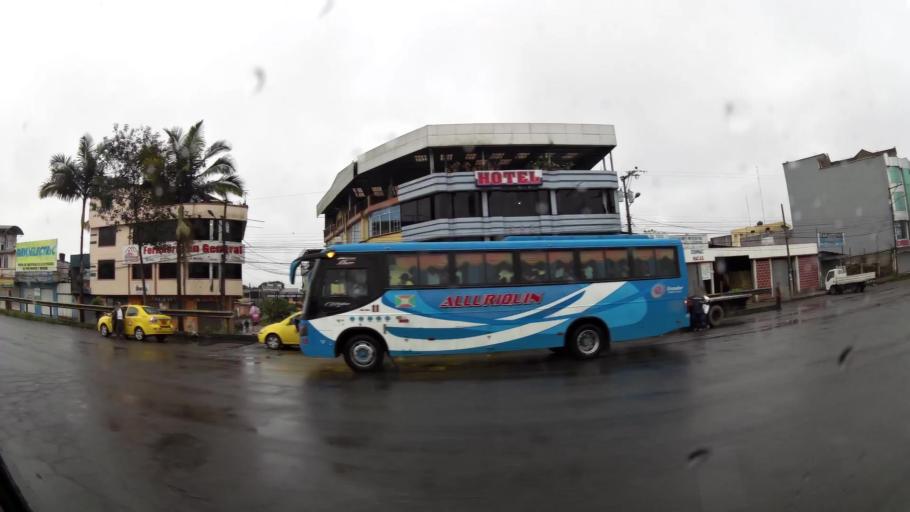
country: EC
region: Santo Domingo de los Tsachilas
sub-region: Canton Santo Domingo de los Colorados
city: Santo Domingo de los Colorados
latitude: -0.2337
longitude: -79.1679
